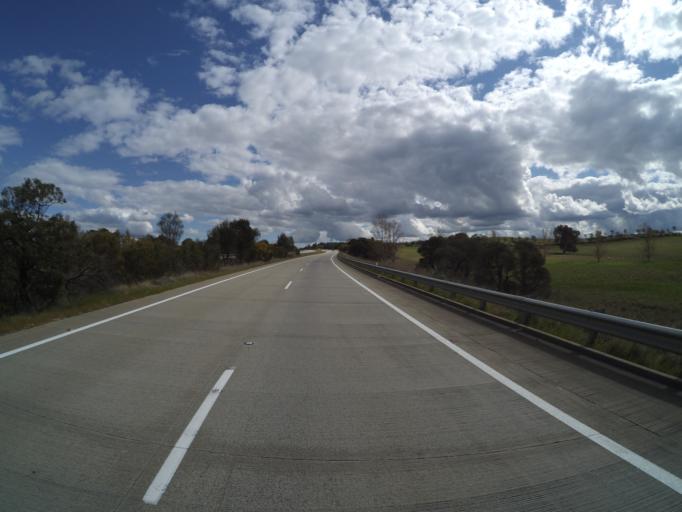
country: AU
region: New South Wales
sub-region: Yass Valley
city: Murrumbateman
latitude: -34.7917
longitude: 149.1712
